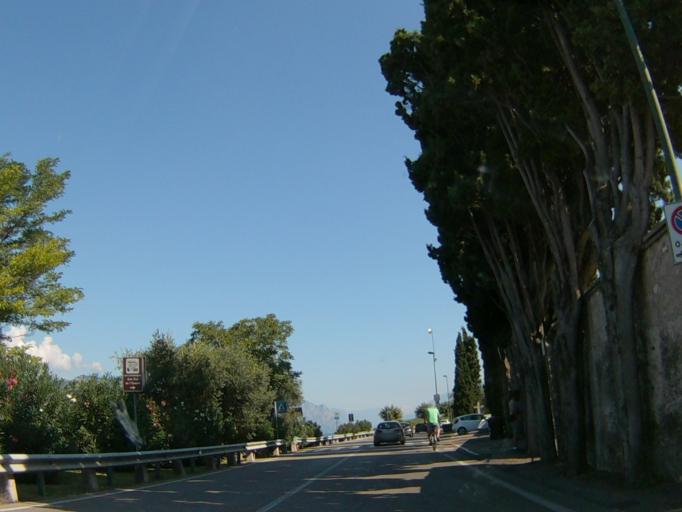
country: IT
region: Veneto
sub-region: Provincia di Verona
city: Brenzone
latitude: 45.6778
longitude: 10.7406
